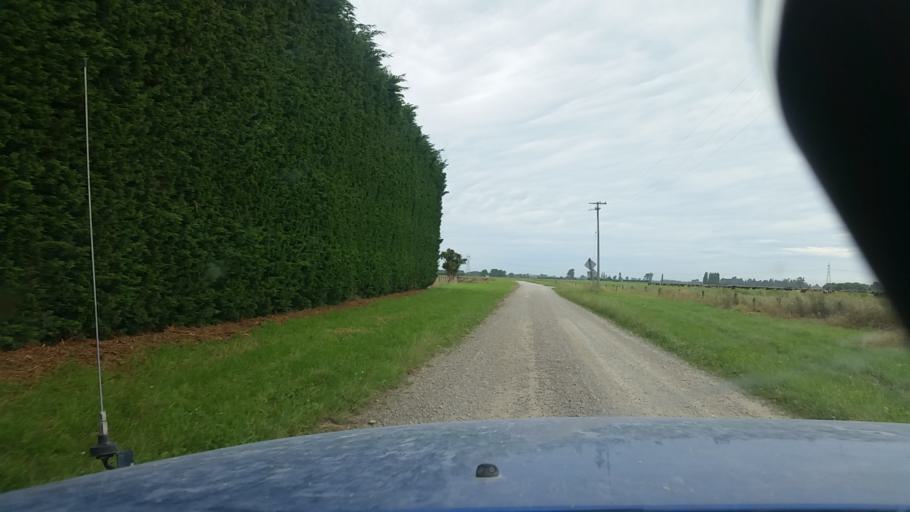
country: NZ
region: Canterbury
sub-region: Ashburton District
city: Ashburton
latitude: -43.8150
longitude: 171.6272
